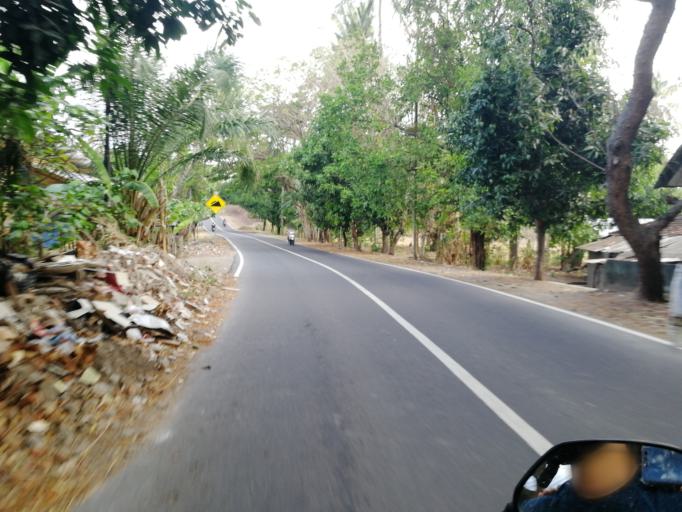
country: ID
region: West Nusa Tenggara
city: Karangsubagan
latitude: -8.4538
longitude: 116.0396
